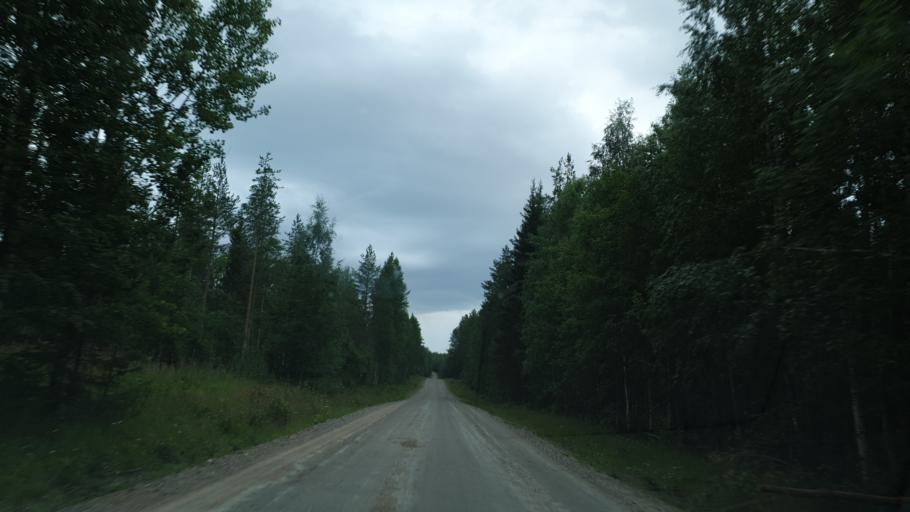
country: FI
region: Kainuu
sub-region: Kehys-Kainuu
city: Kuhmo
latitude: 64.1951
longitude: 29.3685
